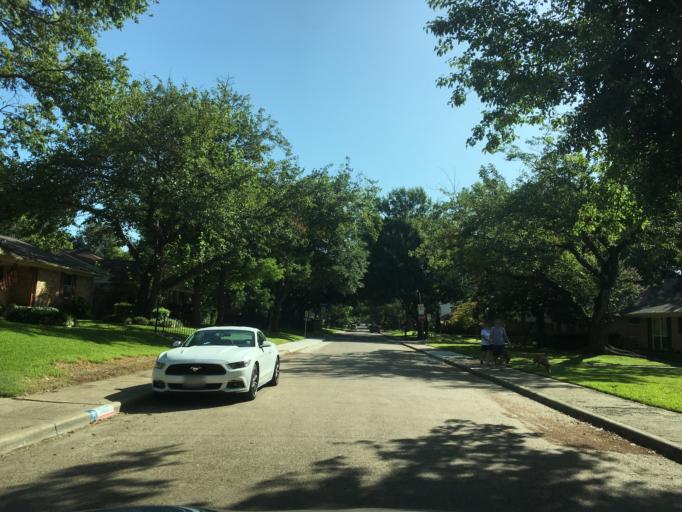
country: US
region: Texas
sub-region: Dallas County
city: Richardson
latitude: 32.8741
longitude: -96.7267
